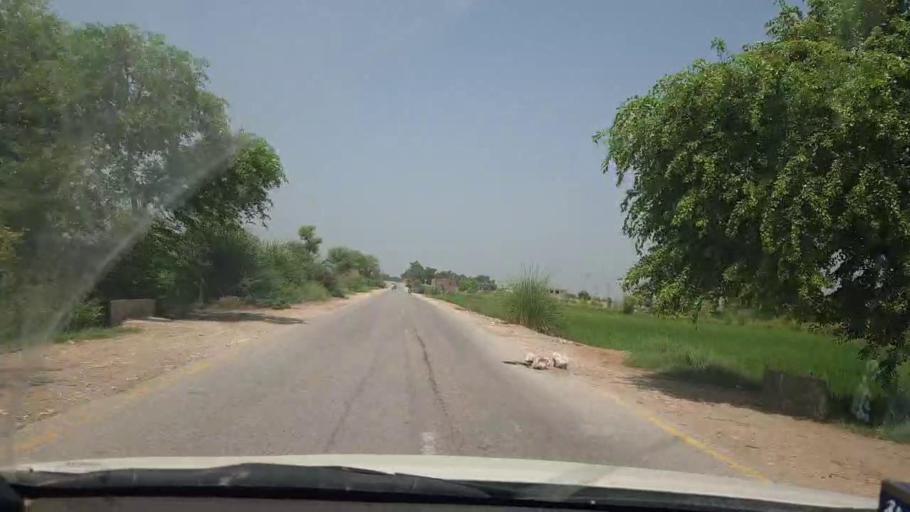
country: PK
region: Sindh
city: Shikarpur
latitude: 27.9542
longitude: 68.6687
